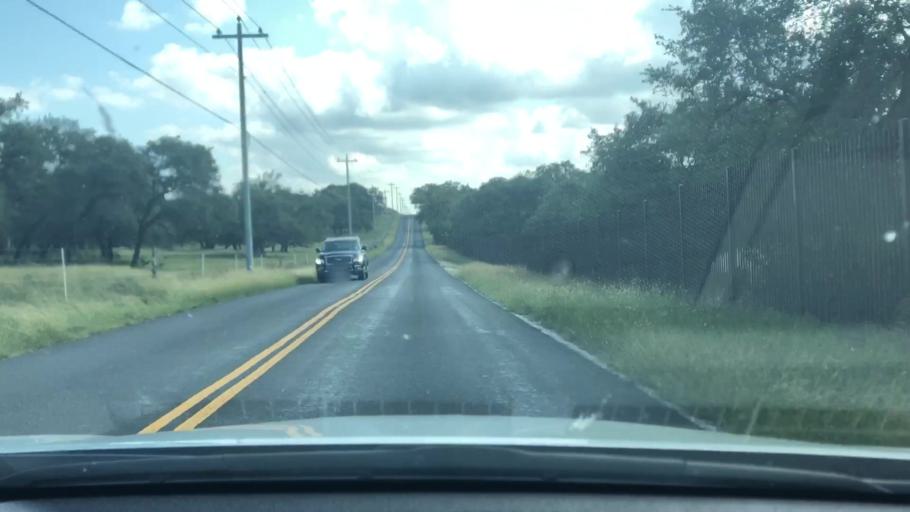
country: US
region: Texas
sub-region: Bexar County
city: Fair Oaks Ranch
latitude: 29.7794
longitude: -98.6266
